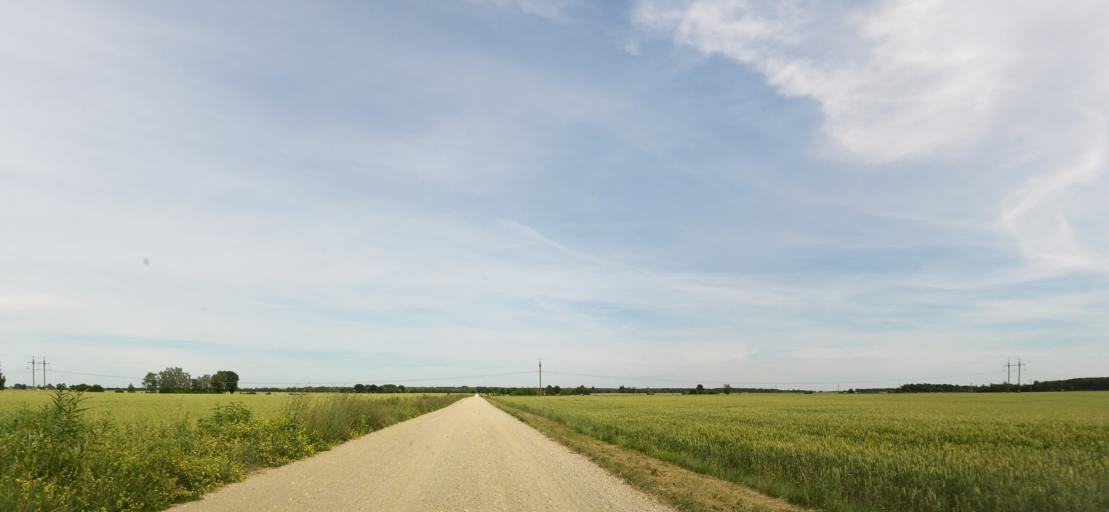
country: LT
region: Panevezys
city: Pasvalys
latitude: 55.9661
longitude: 24.3089
